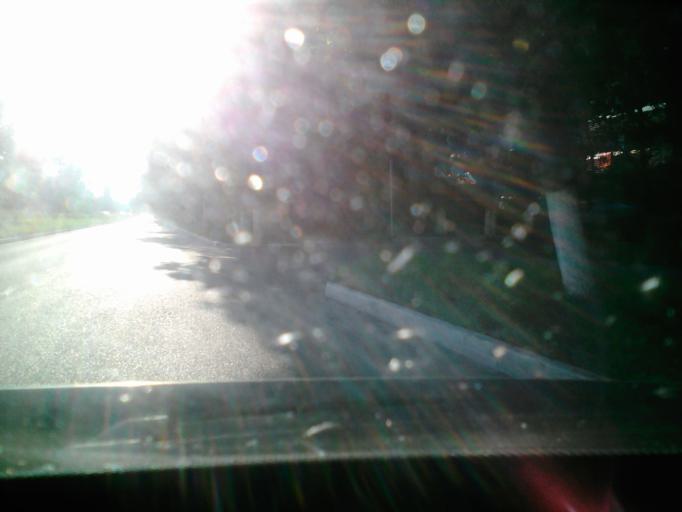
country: RU
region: Kursk
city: Kurchatov
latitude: 51.6574
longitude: 35.6550
